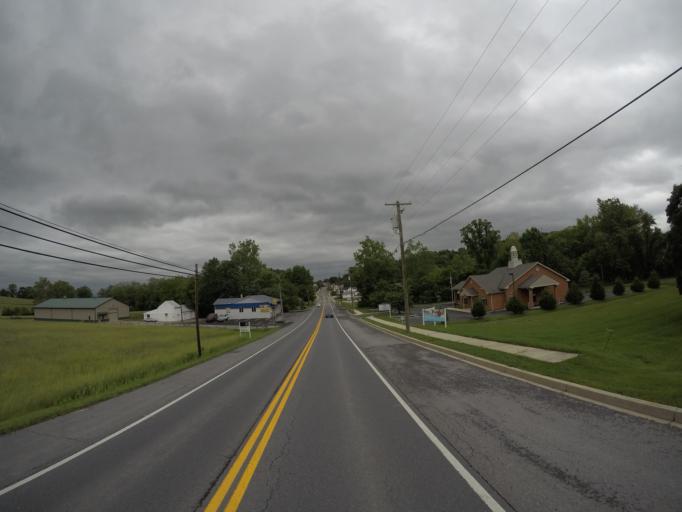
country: US
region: Maryland
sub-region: Washington County
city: Boonsboro
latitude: 39.4984
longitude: -77.6460
